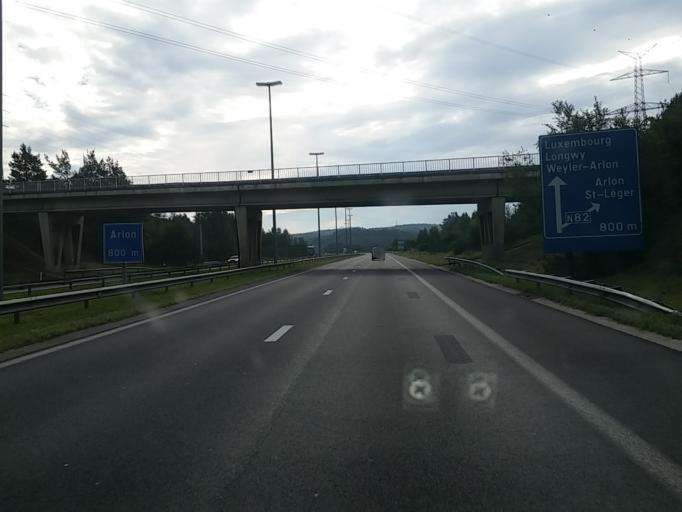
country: BE
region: Wallonia
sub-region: Province du Luxembourg
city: Arlon
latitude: 49.6790
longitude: 5.7603
